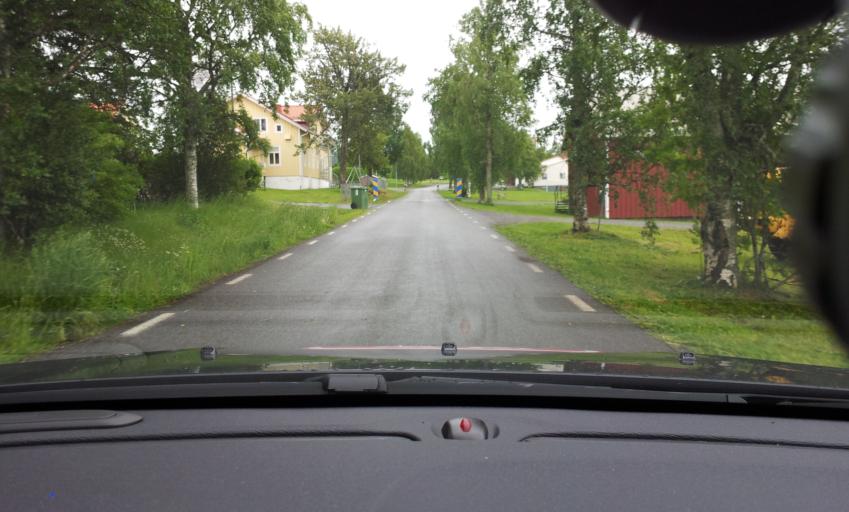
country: SE
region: Jaemtland
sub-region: Krokoms Kommun
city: Krokom
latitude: 63.3677
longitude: 14.4818
